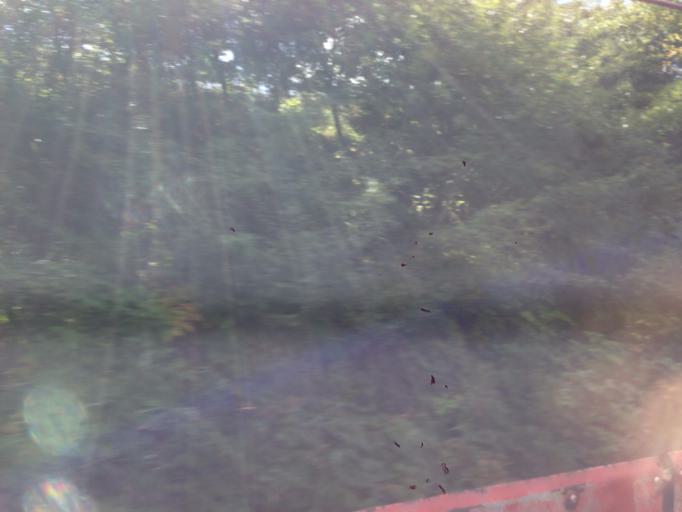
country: DE
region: Schleswig-Holstein
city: Sylt-Ost
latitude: 54.8710
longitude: 8.4540
